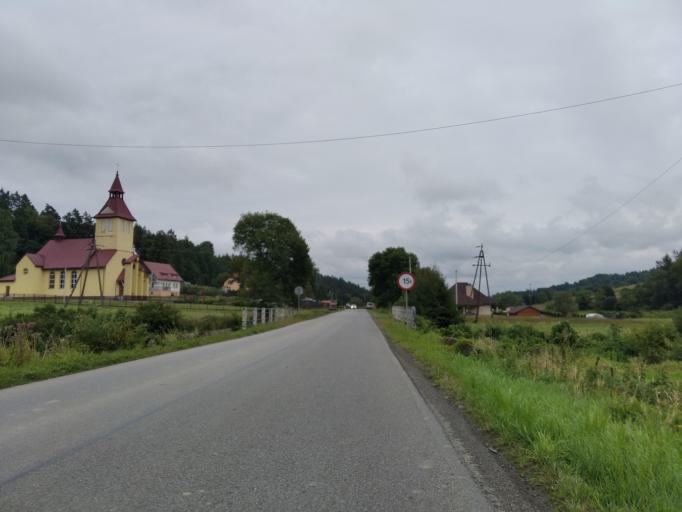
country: PL
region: Subcarpathian Voivodeship
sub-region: Powiat przemyski
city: Bircza
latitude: 49.6994
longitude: 22.3761
